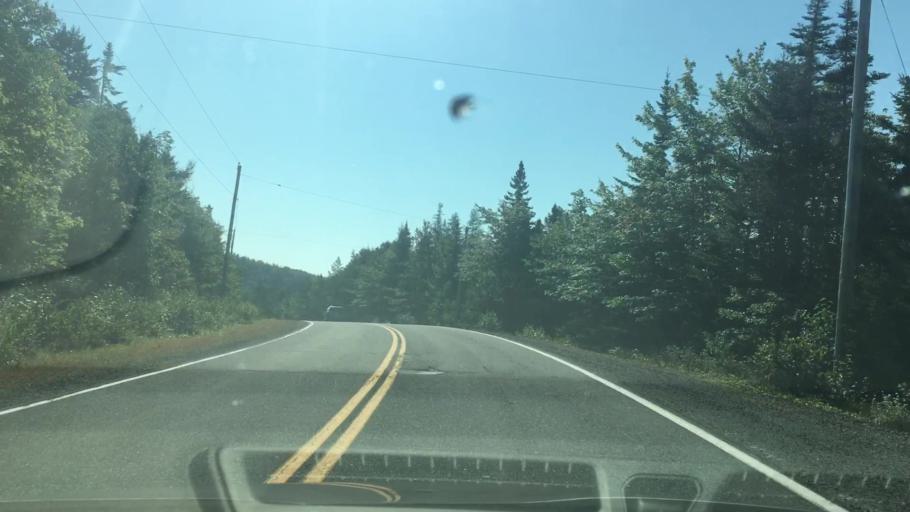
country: CA
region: Nova Scotia
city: Cole Harbour
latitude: 44.8082
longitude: -62.8341
